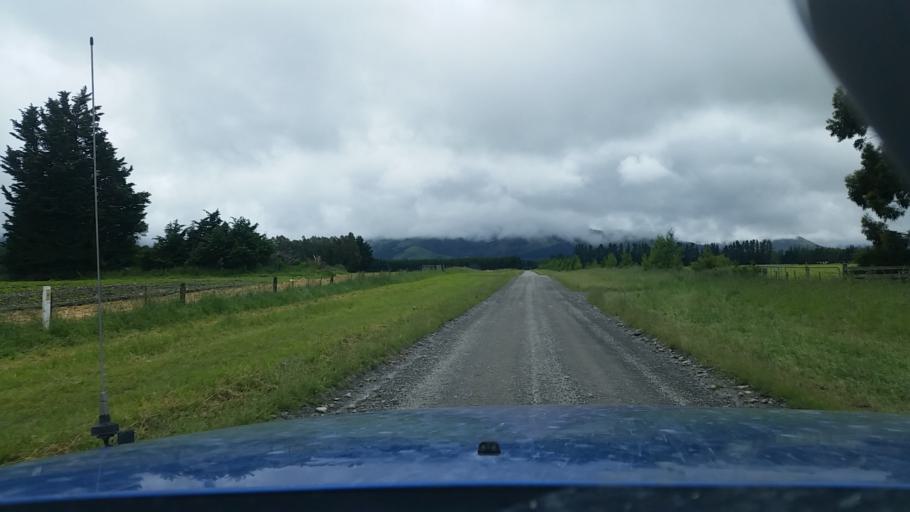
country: NZ
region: Canterbury
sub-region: Ashburton District
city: Methven
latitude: -43.6477
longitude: 171.4772
